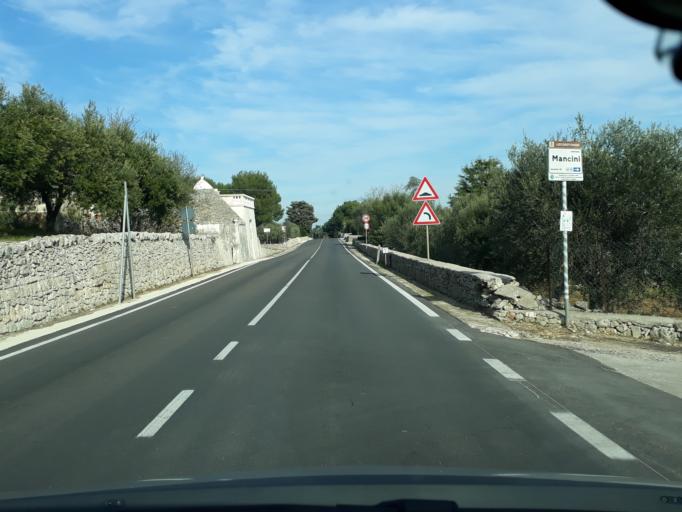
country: IT
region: Apulia
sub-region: Provincia di Brindisi
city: Lamie di Olimpie-Selva
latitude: 40.7870
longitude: 17.3425
